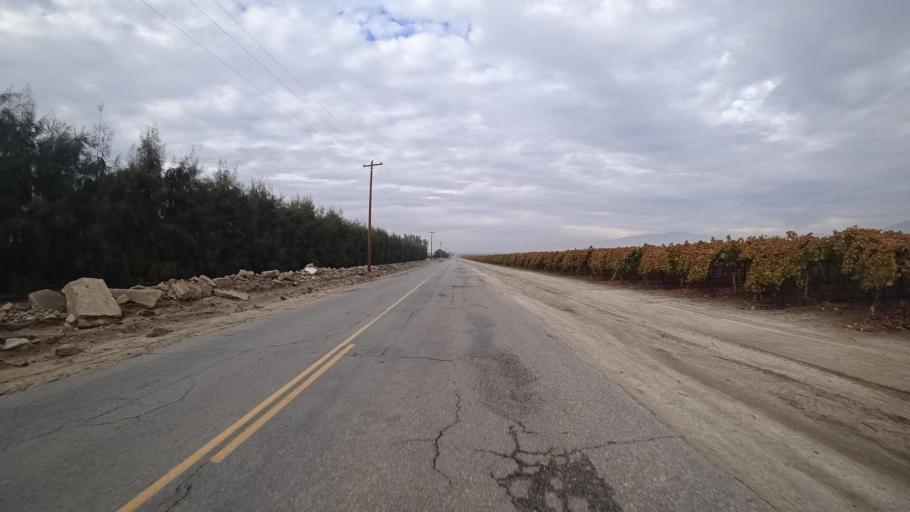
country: US
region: California
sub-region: Kern County
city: Arvin
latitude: 35.1525
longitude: -118.8235
